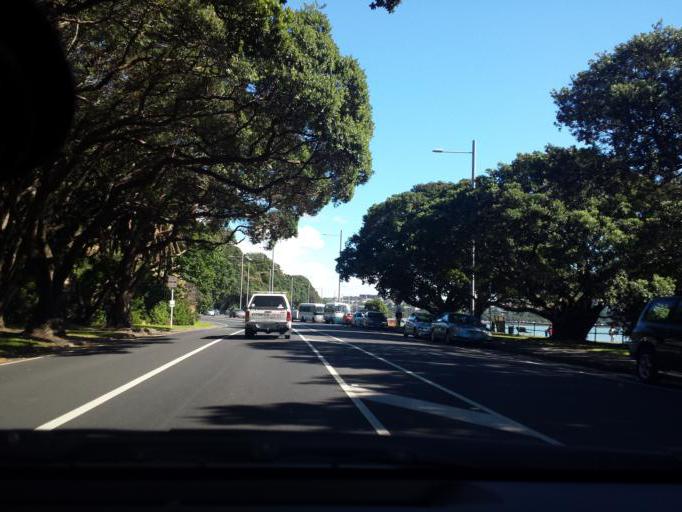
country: NZ
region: Auckland
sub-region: Auckland
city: Auckland
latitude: -36.8510
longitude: 174.8096
